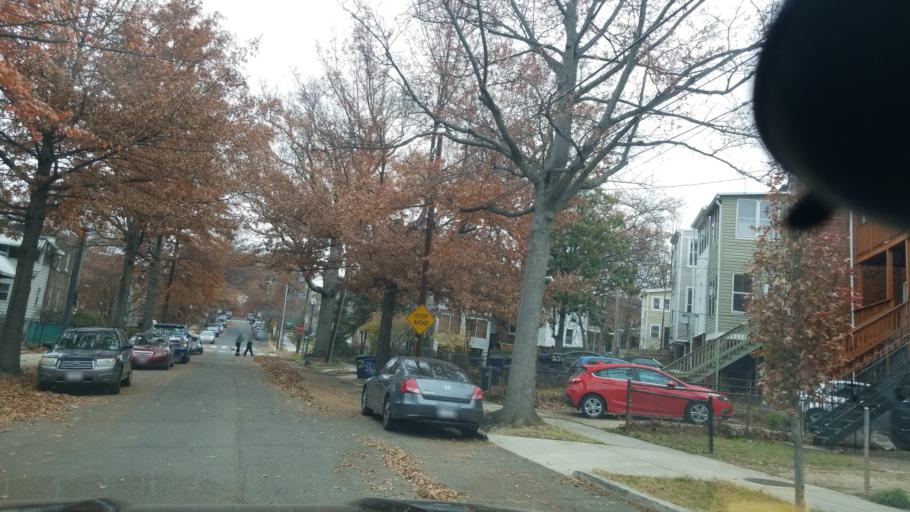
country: US
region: Maryland
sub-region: Prince George's County
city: Chillum
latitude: 38.9403
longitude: -77.0153
